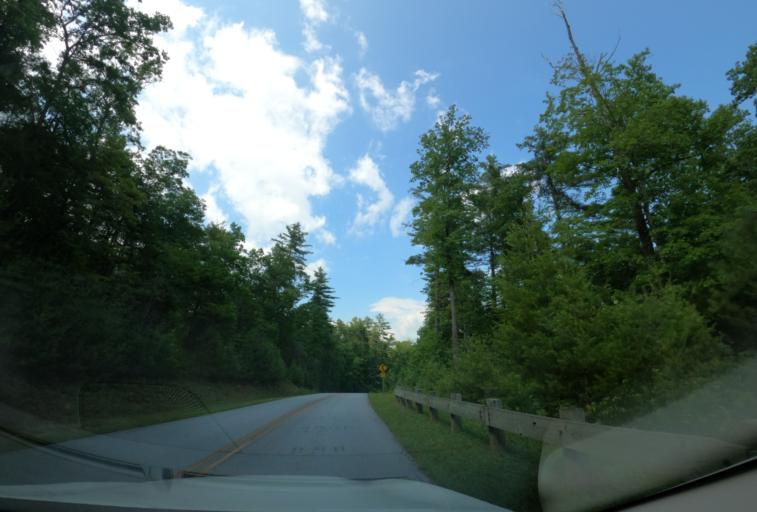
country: US
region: North Carolina
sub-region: Transylvania County
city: Brevard
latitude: 35.1017
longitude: -82.9531
